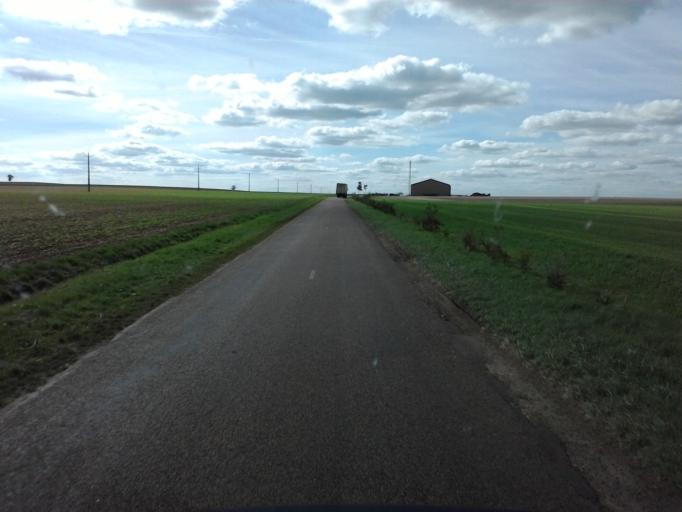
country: FR
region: Bourgogne
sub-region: Departement de la Cote-d'Or
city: Montbard
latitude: 47.7330
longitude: 4.4438
